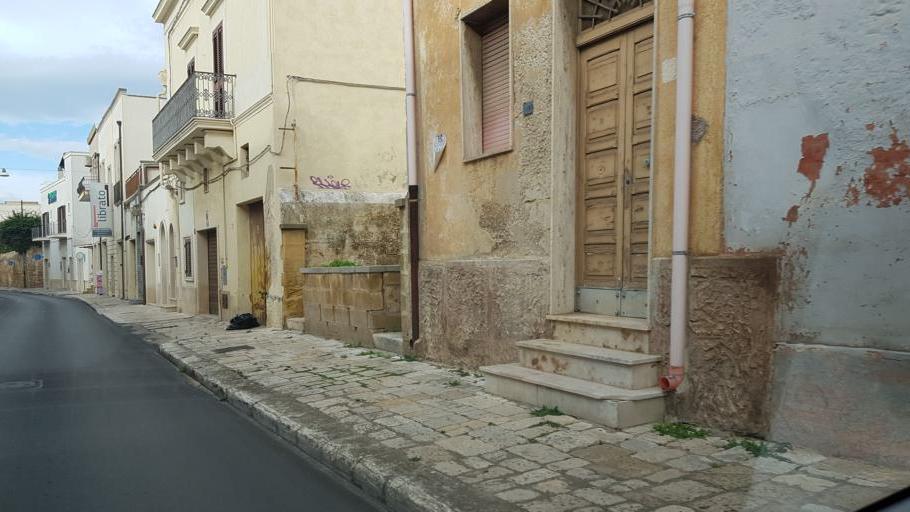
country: IT
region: Apulia
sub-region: Provincia di Brindisi
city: Mesagne
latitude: 40.5598
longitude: 17.8108
